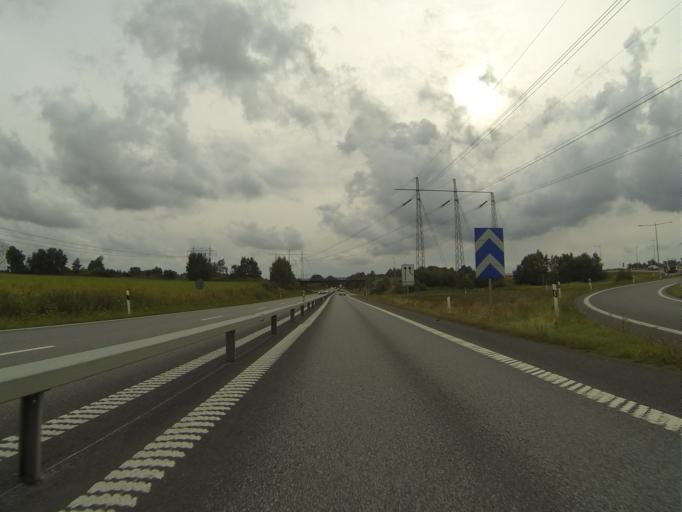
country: SE
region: Skane
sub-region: Horby Kommun
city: Hoerby
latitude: 55.8607
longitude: 13.6430
